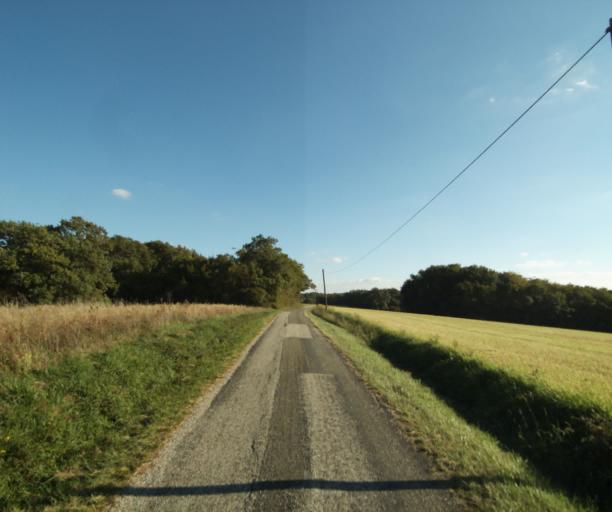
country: FR
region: Midi-Pyrenees
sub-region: Departement du Gers
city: Eauze
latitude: 43.7868
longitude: 0.1214
